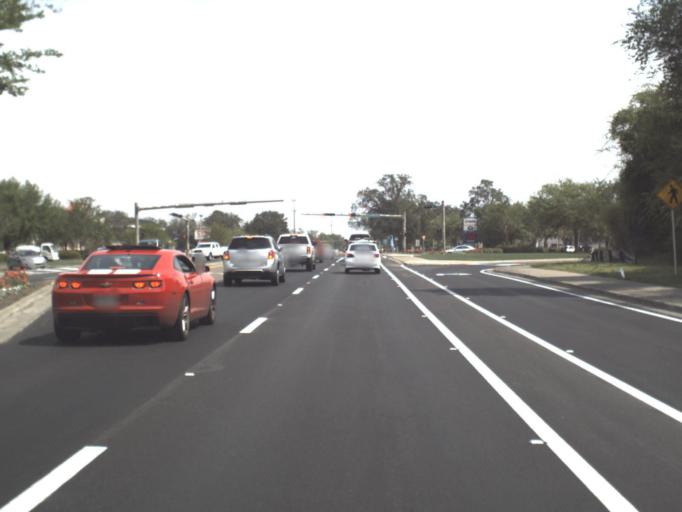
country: US
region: Florida
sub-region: Okaloosa County
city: Niceville
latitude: 30.4848
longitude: -86.4183
